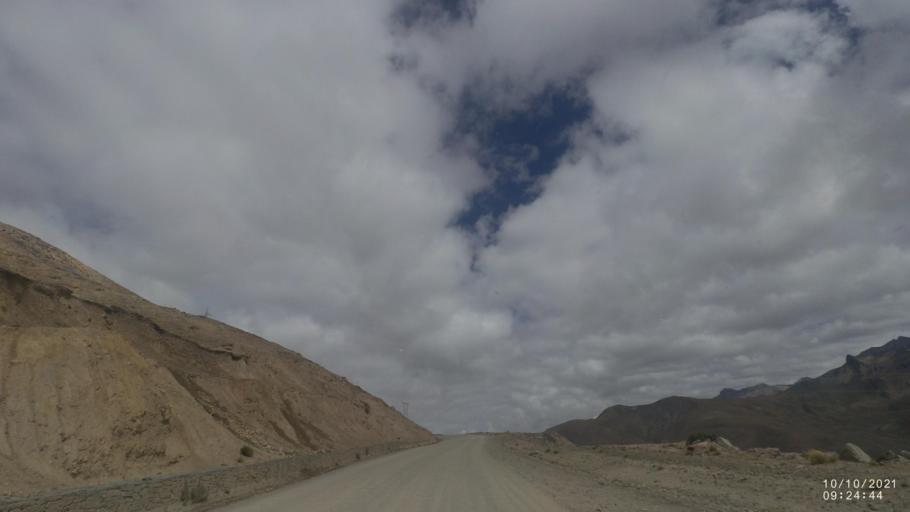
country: BO
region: La Paz
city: Quime
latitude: -17.0912
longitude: -67.3108
